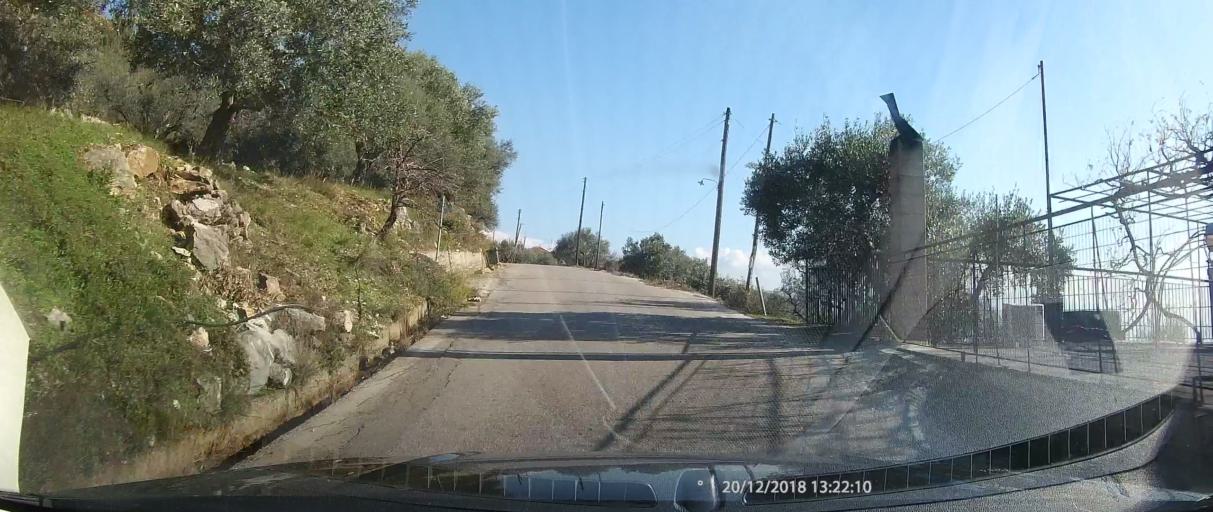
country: GR
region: West Greece
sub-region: Nomos Aitolias kai Akarnanias
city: Paravola
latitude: 38.6160
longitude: 21.5639
